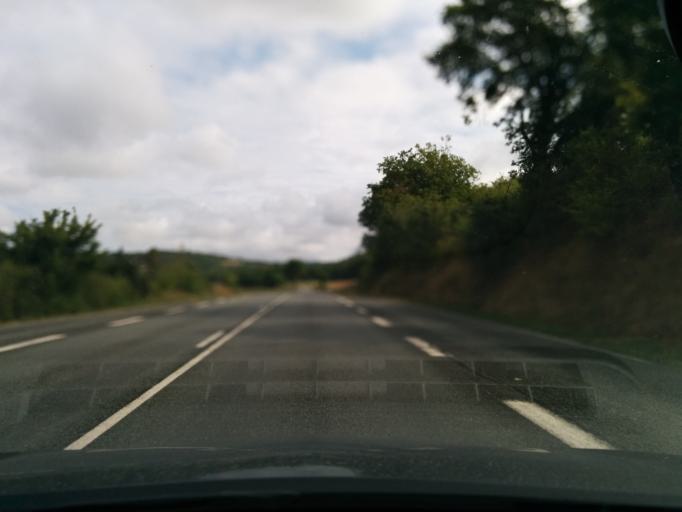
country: FR
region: Midi-Pyrenees
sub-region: Departement du Lot
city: Le Vigan
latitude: 44.6819
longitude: 1.4829
